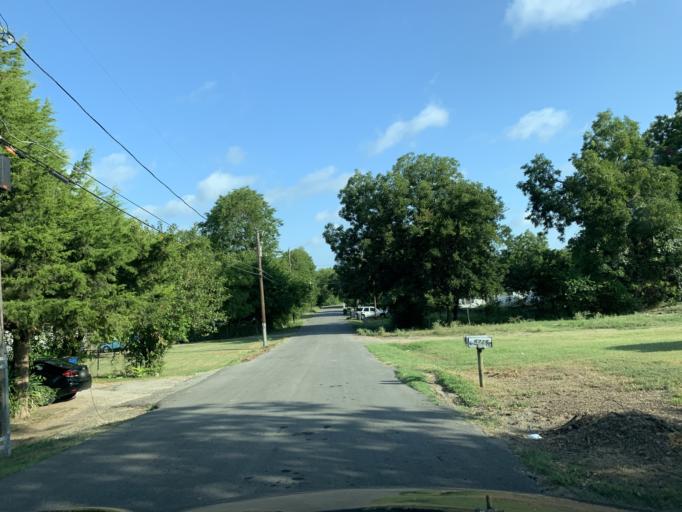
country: US
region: Texas
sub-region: Dallas County
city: Hutchins
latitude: 32.6785
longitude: -96.7668
